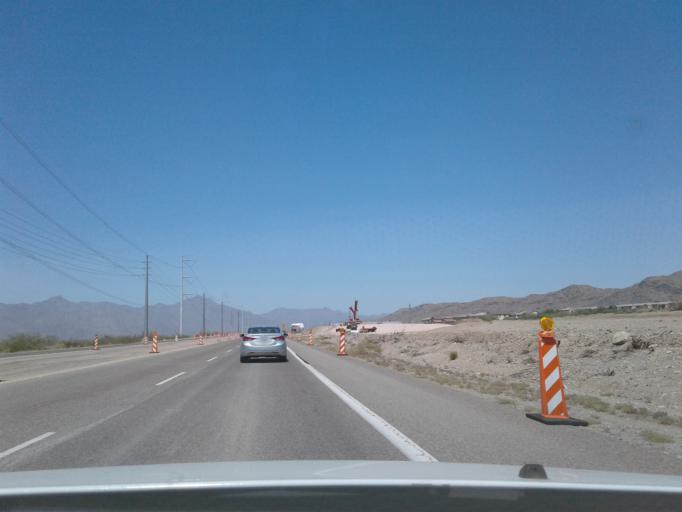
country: US
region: Arizona
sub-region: Maricopa County
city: Laveen
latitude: 33.2911
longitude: -112.0921
